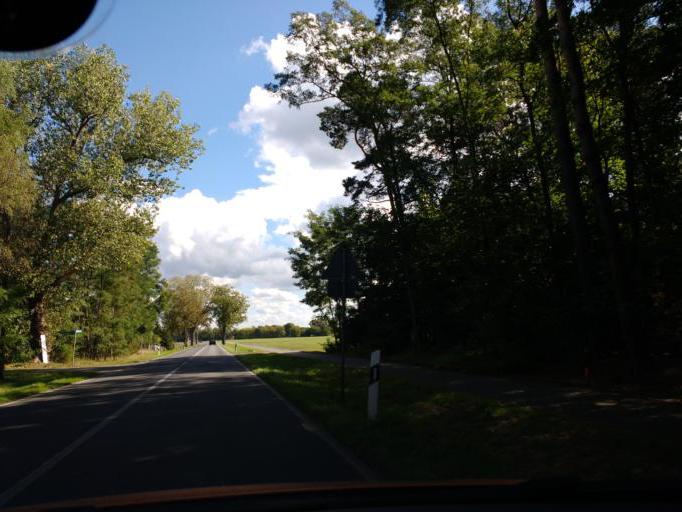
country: DE
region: Brandenburg
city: Bestensee
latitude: 52.2423
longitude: 13.6929
